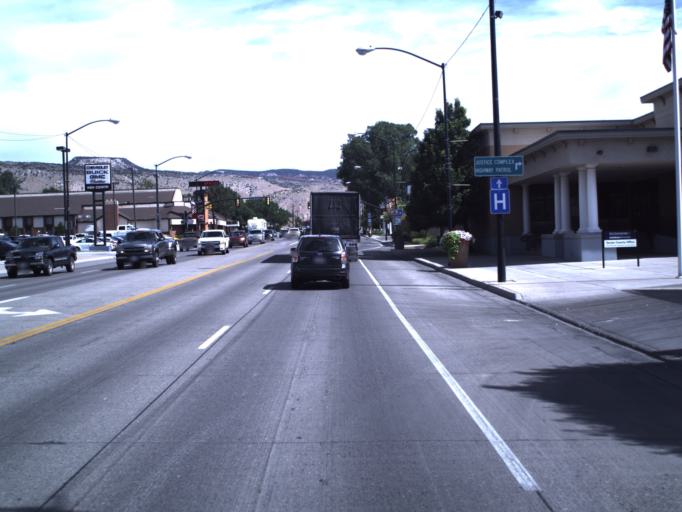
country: US
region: Utah
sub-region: Sevier County
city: Richfield
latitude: 38.7710
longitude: -112.0847
